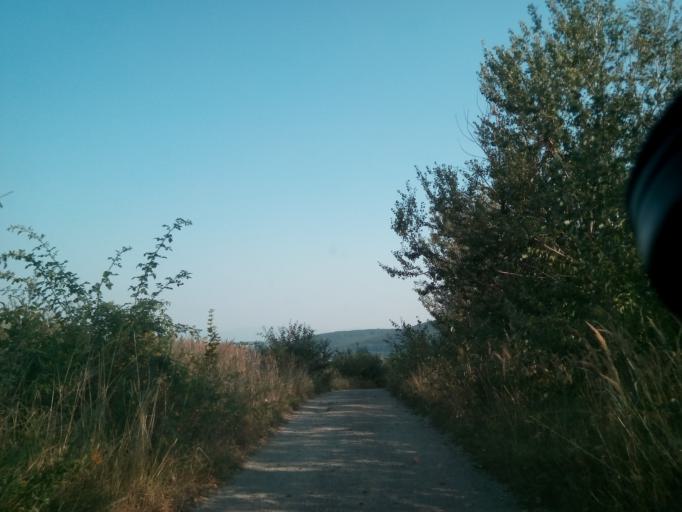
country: SK
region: Kosicky
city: Moldava nad Bodvou
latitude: 48.7323
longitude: 21.0994
